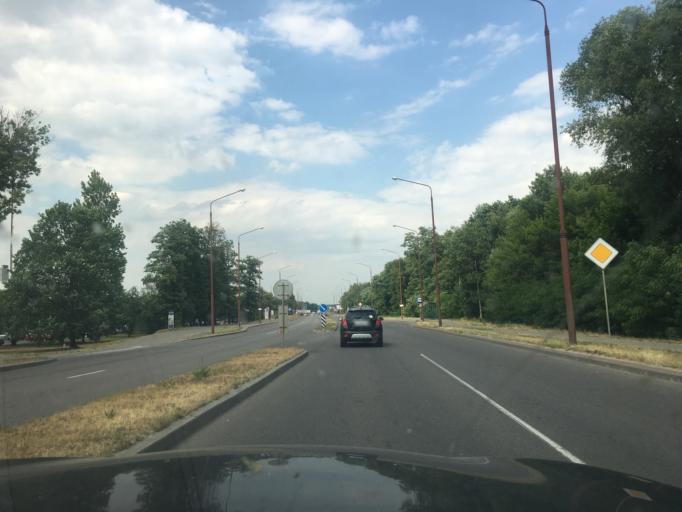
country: BY
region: Brest
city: Brest
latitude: 52.1428
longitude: 23.6817
